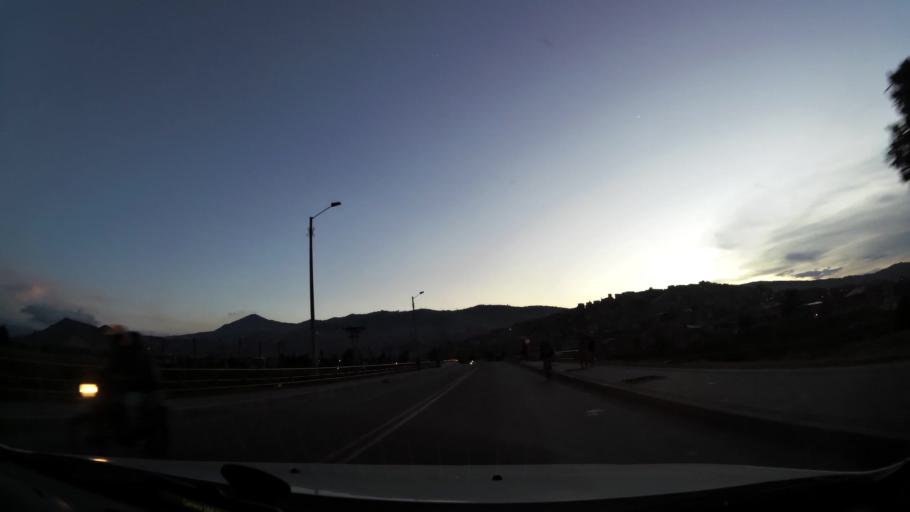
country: CO
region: Bogota D.C.
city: Bogota
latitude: 4.5595
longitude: -74.1337
